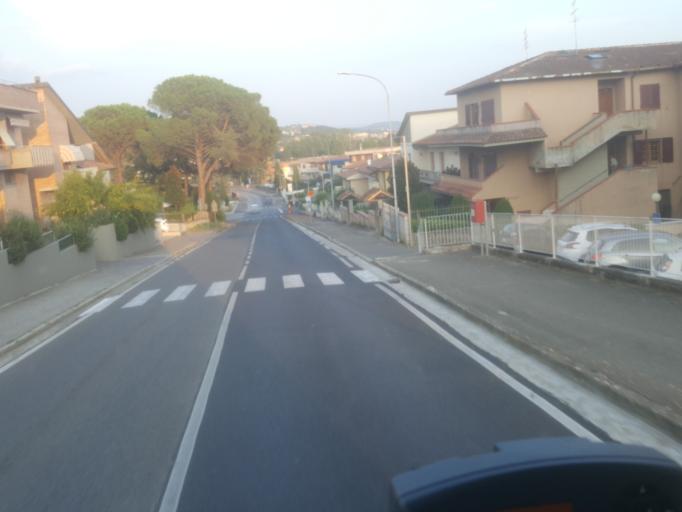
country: IT
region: Tuscany
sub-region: Province of Florence
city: Certaldo
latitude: 43.5450
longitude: 11.0288
